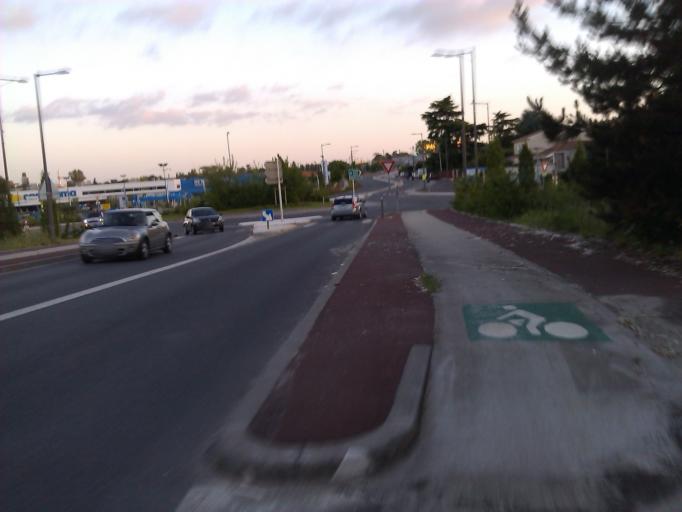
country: FR
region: Aquitaine
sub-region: Departement de la Gironde
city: Lormont
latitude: 44.8847
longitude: -0.5083
